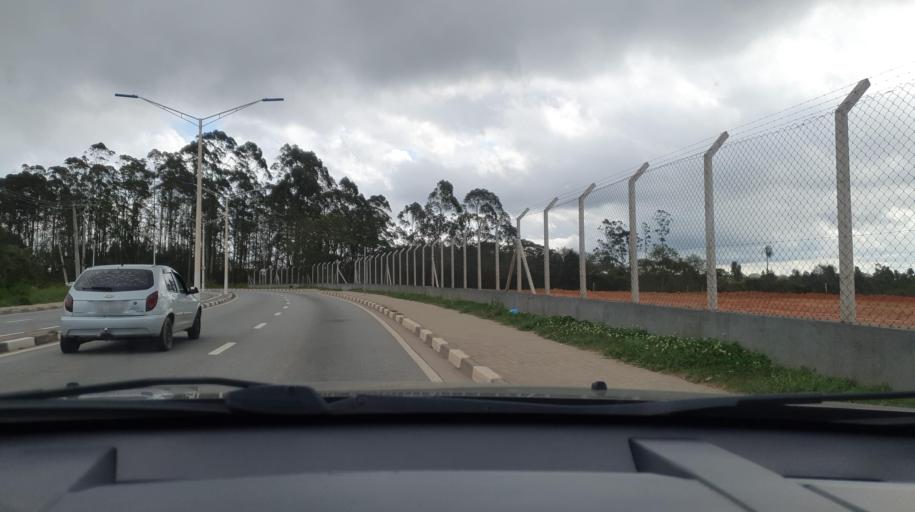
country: BR
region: Sao Paulo
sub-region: Vargem Grande Paulista
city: Vargem Grande Paulista
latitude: -23.6717
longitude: -47.0140
